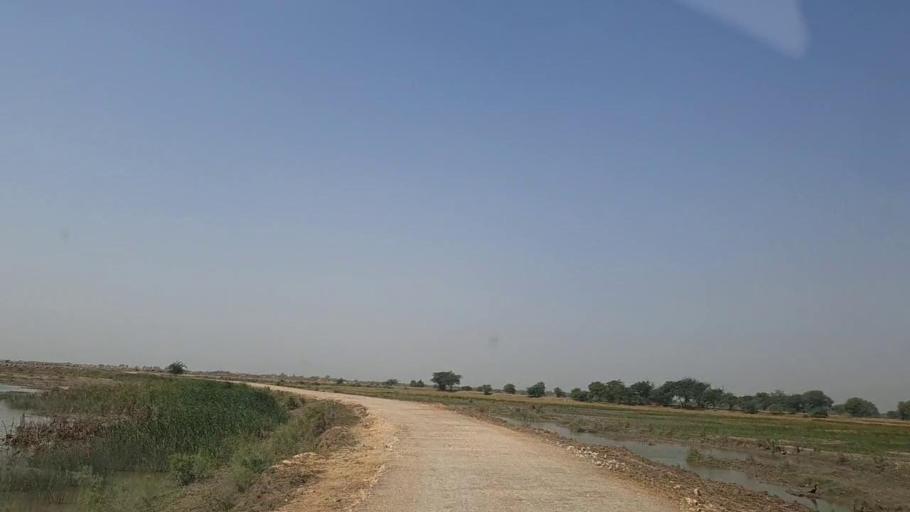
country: PK
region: Sindh
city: Daro Mehar
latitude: 24.7536
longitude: 68.1388
